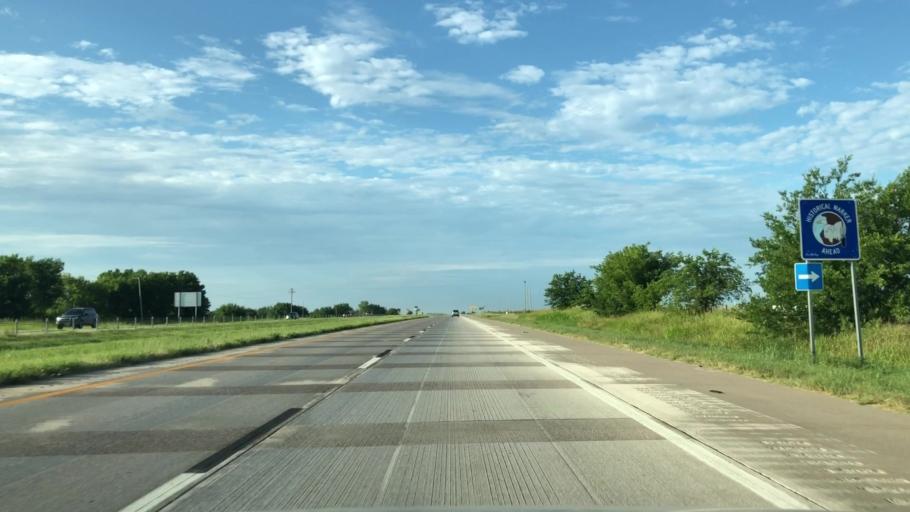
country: US
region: Oklahoma
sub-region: Osage County
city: Skiatook
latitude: 36.4263
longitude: -95.9206
